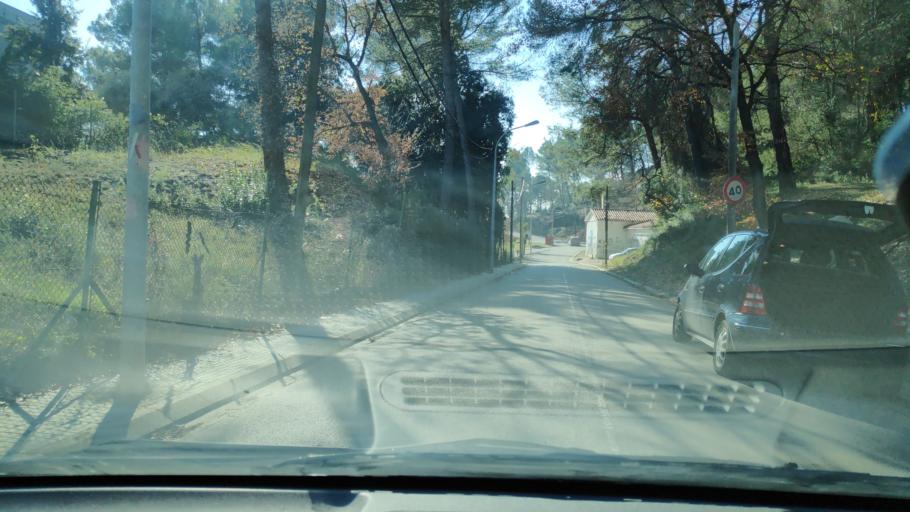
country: ES
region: Catalonia
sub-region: Provincia de Barcelona
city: Sant Quirze del Valles
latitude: 41.5062
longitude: 2.0797
